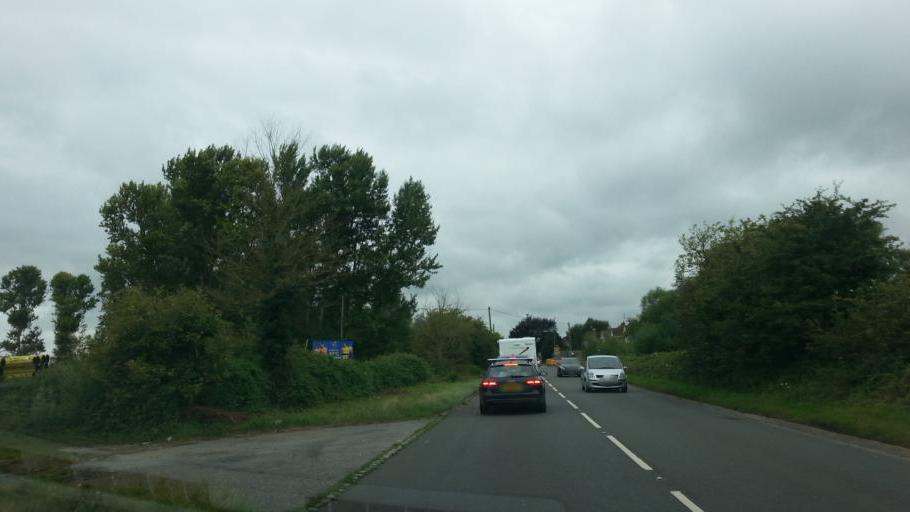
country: GB
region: England
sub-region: Wiltshire
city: Lacock
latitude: 51.3985
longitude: -2.1298
